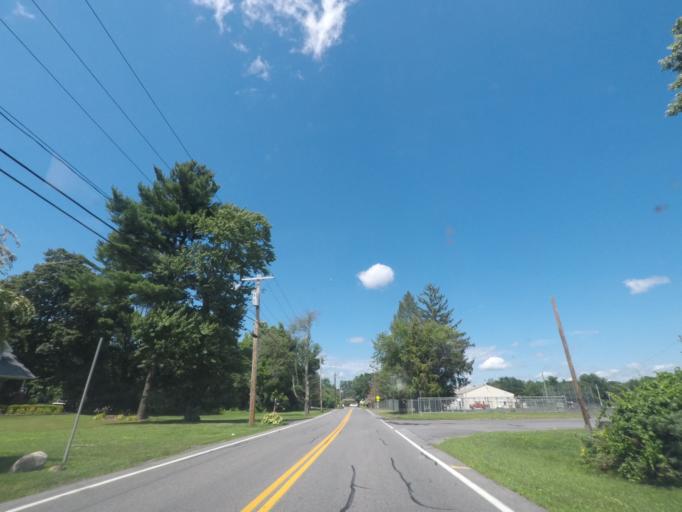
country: US
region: New York
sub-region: Schenectady County
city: Rotterdam
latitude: 42.7709
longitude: -73.9598
